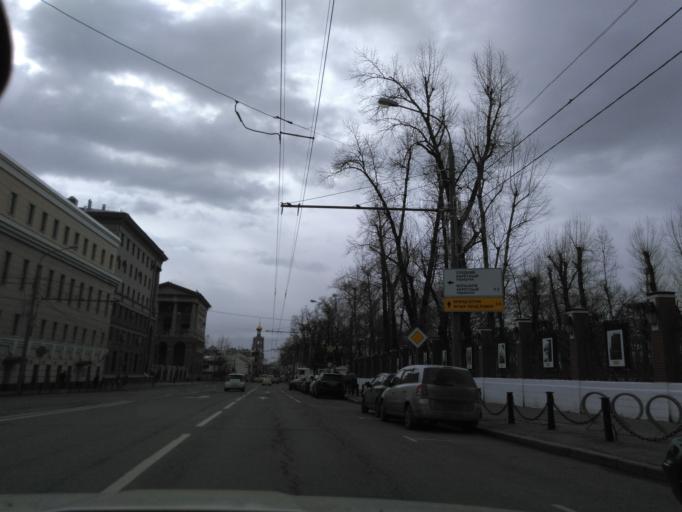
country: RU
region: Moscow
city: Moscow
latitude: 55.7709
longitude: 37.6111
